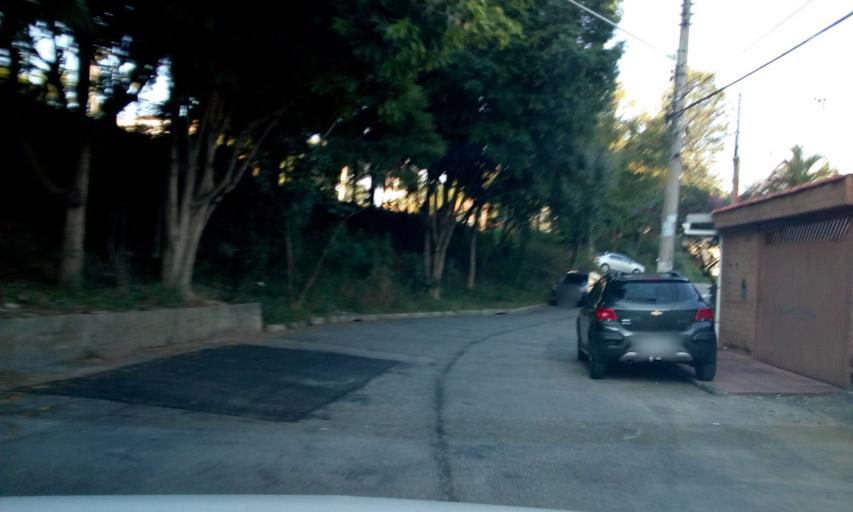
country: BR
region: Sao Paulo
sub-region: Sao Paulo
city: Sao Paulo
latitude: -23.4900
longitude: -46.6129
